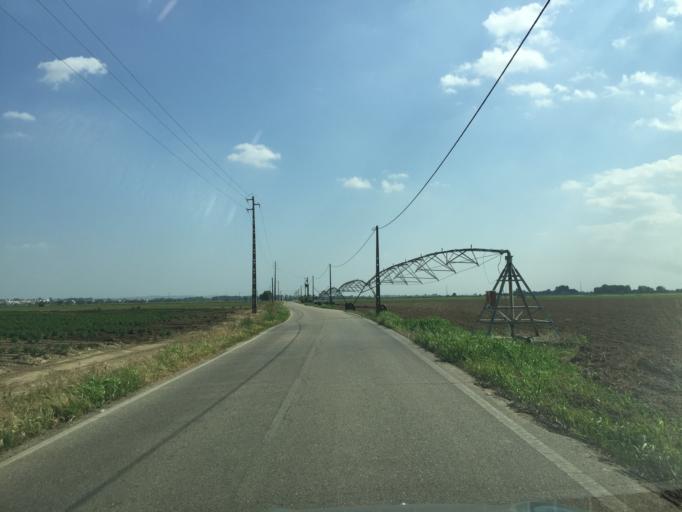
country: PT
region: Santarem
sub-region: Alpiarca
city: Alpiarca
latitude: 39.2850
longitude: -8.5934
